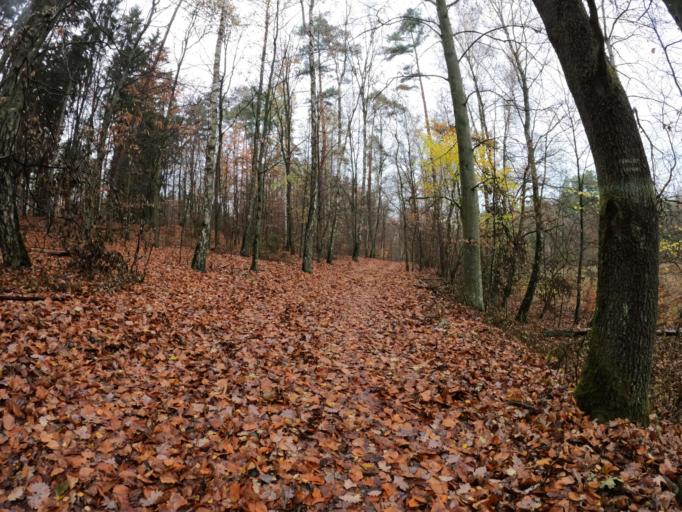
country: PL
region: West Pomeranian Voivodeship
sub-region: Powiat walecki
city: Tuczno
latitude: 53.2670
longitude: 16.2551
